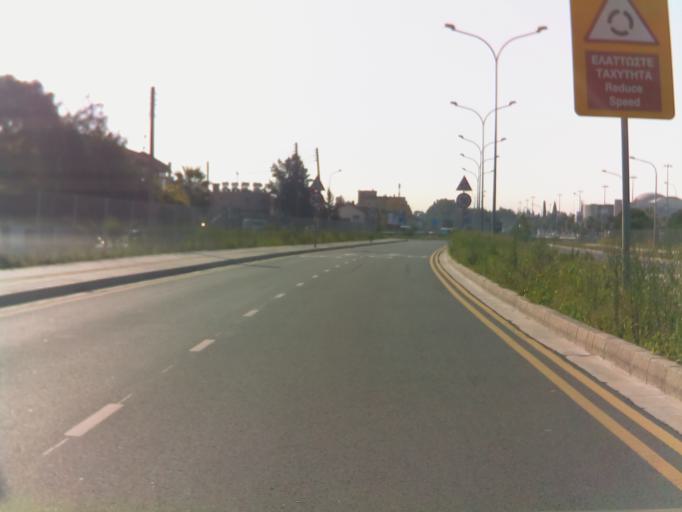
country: CY
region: Limassol
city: Ypsonas
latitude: 34.6584
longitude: 32.9965
